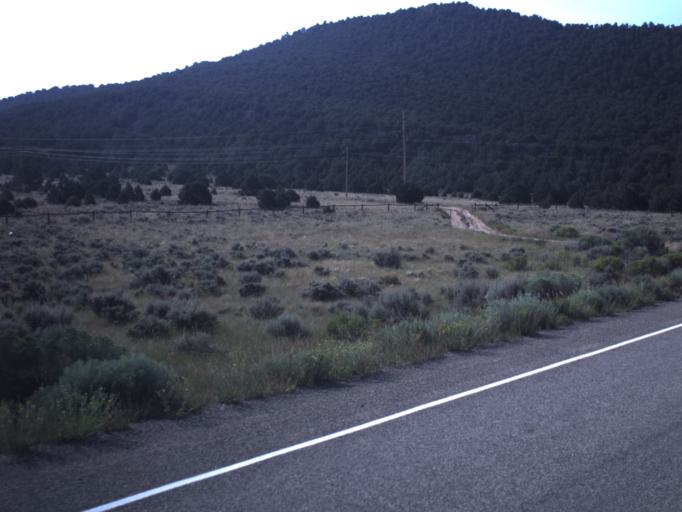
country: US
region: Utah
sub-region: Daggett County
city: Manila
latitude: 40.9603
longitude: -109.4697
